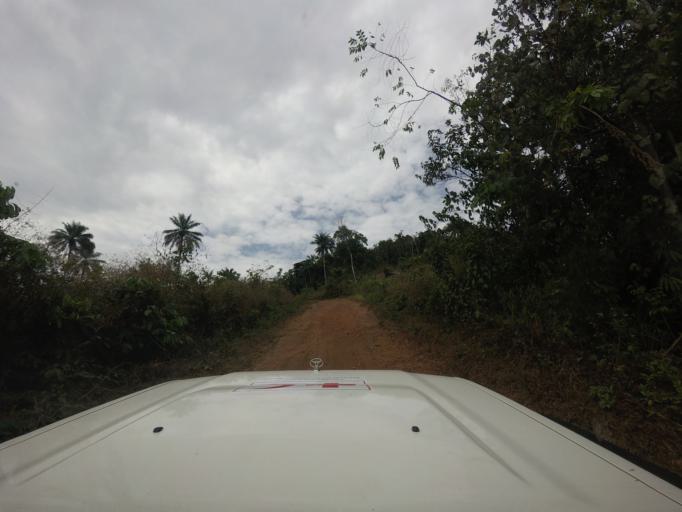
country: SL
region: Eastern Province
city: Buedu
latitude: 8.2462
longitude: -10.2583
